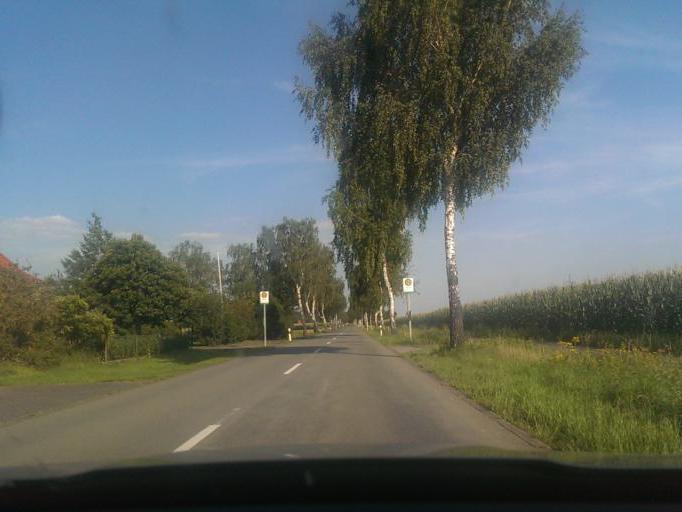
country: DE
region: North Rhine-Westphalia
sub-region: Regierungsbezirk Detmold
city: Delbruck
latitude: 51.7370
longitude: 8.6041
